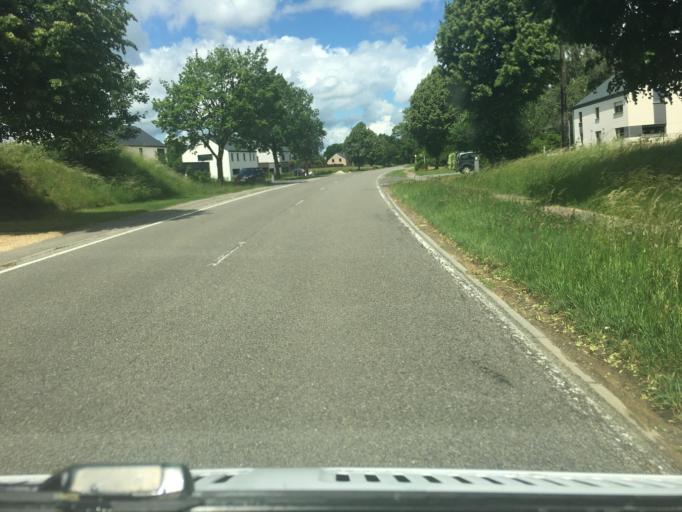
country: BE
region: Wallonia
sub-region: Province du Luxembourg
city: Florenville
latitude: 49.6844
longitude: 5.3306
